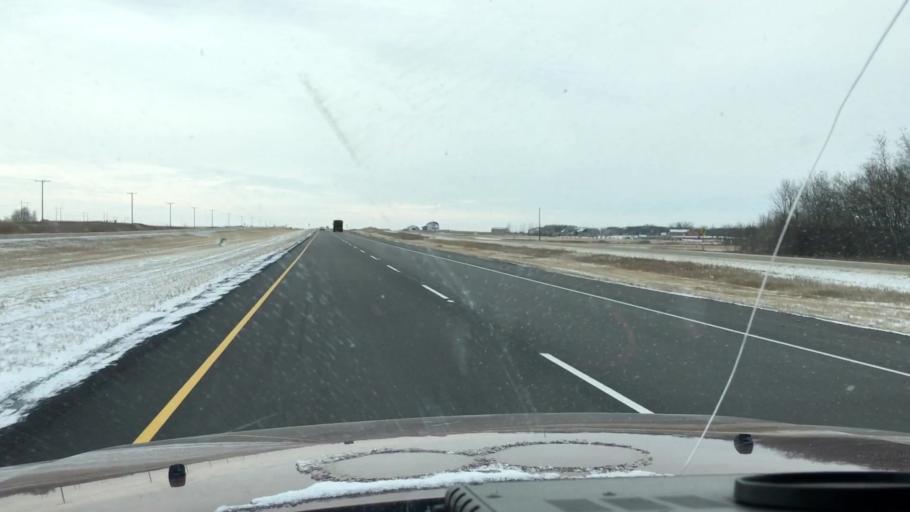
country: CA
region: Saskatchewan
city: Saskatoon
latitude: 51.9351
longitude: -106.5377
